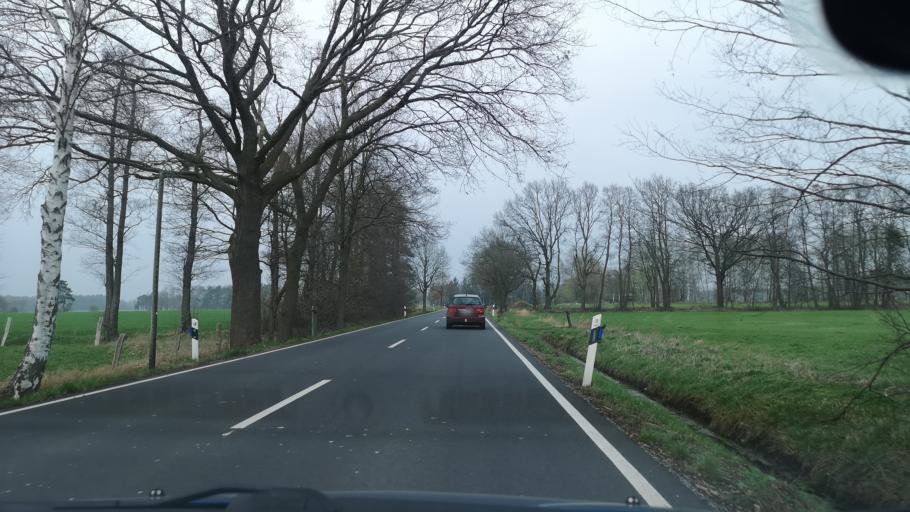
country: DE
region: Lower Saxony
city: Garbsen
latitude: 52.4752
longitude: 9.5358
